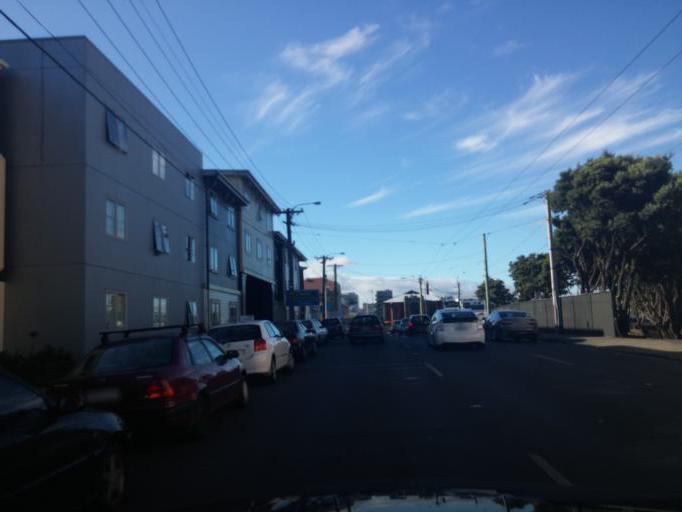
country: NZ
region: Wellington
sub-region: Wellington City
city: Wellington
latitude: -41.2999
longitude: 174.7790
